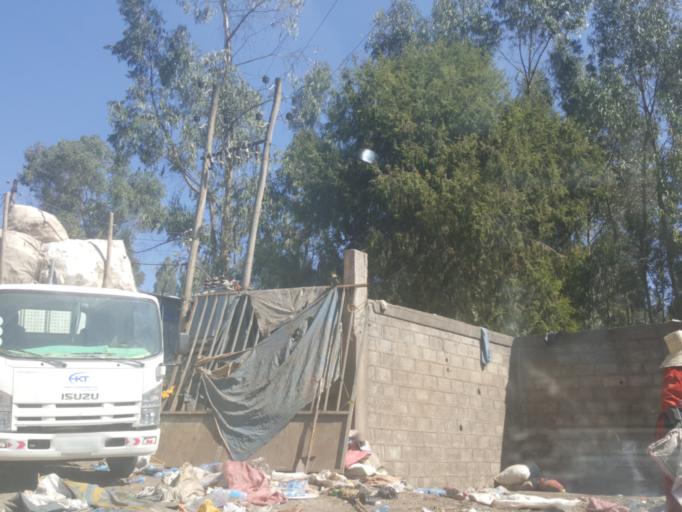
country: ET
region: Adis Abeba
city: Addis Ababa
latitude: 9.0693
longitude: 38.7332
